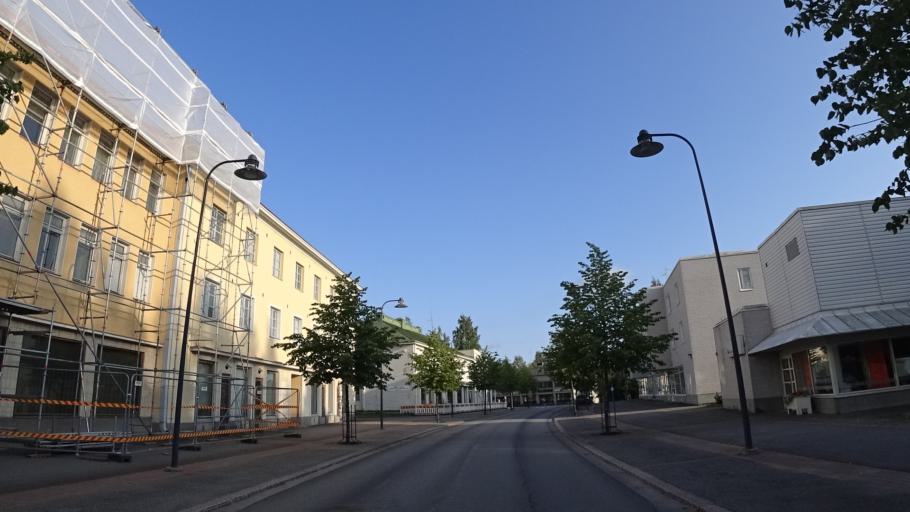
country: FI
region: North Karelia
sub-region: Pielisen Karjala
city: Lieksa
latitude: 63.3157
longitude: 30.0324
